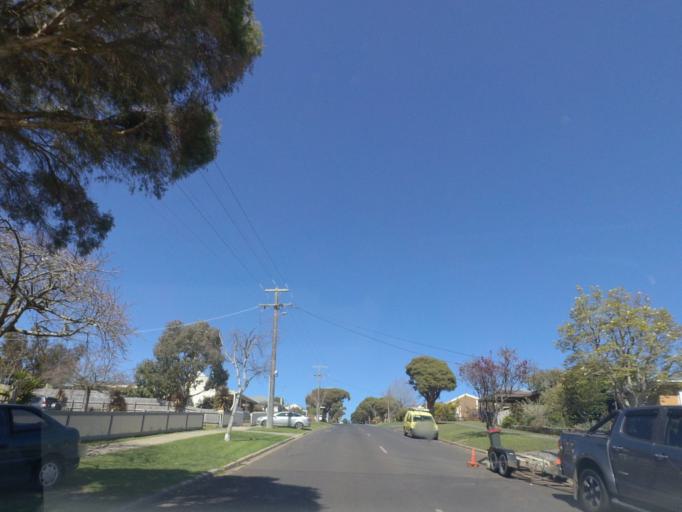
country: AU
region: Victoria
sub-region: Baw Baw
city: Warragul
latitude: -38.1342
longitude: 145.8631
